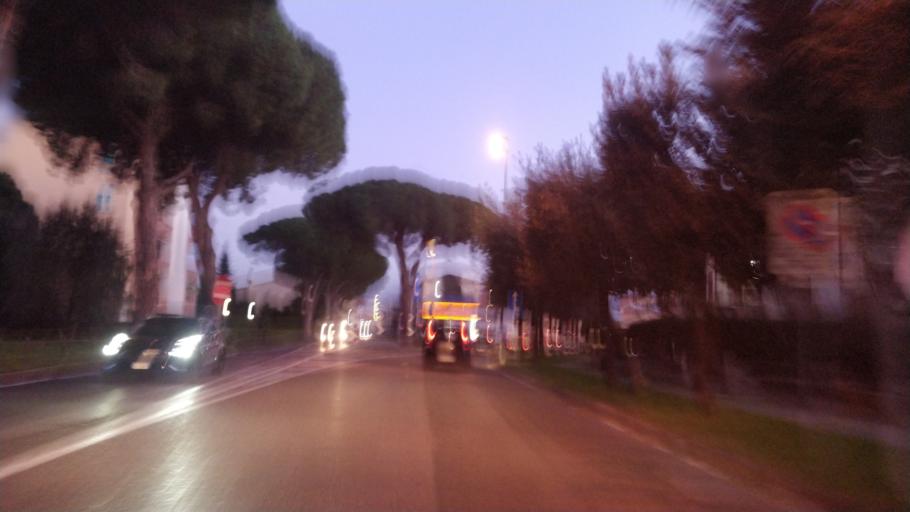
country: IT
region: Tuscany
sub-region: Provincia di Livorno
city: S.P. in Palazzi
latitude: 43.3294
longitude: 10.5026
